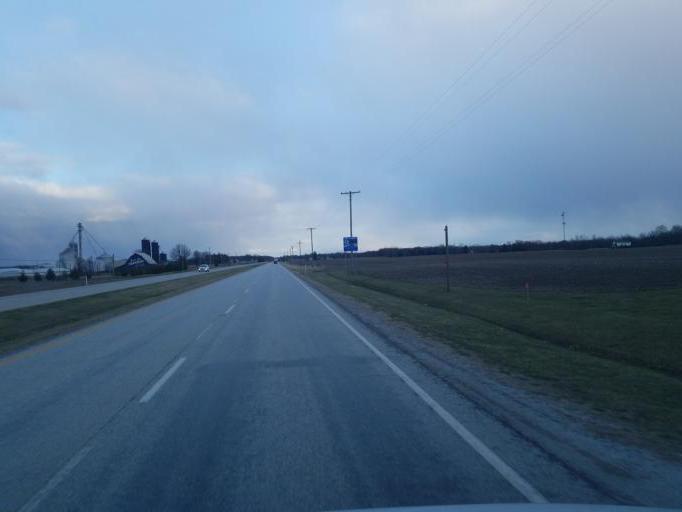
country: US
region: Indiana
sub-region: Henry County
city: Knightstown
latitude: 39.7907
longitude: -85.6342
